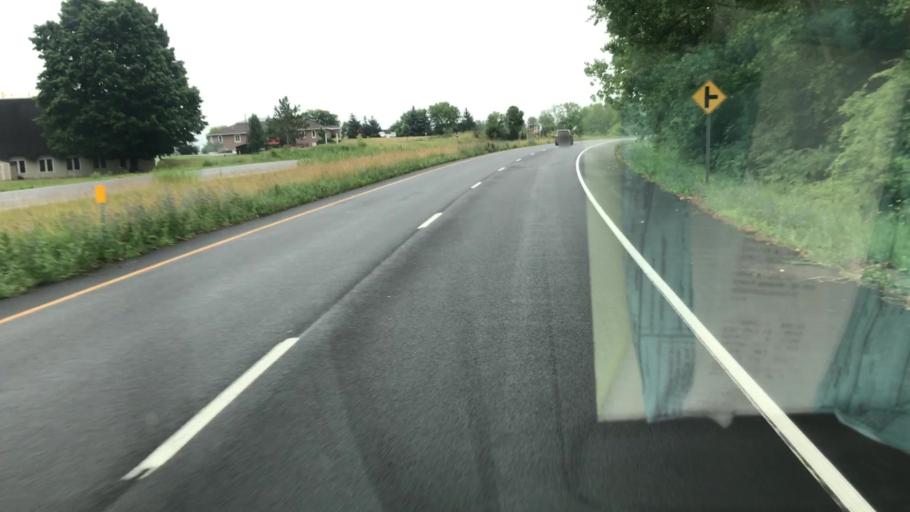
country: US
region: New York
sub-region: Onondaga County
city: Liverpool
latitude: 43.1381
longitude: -76.2081
